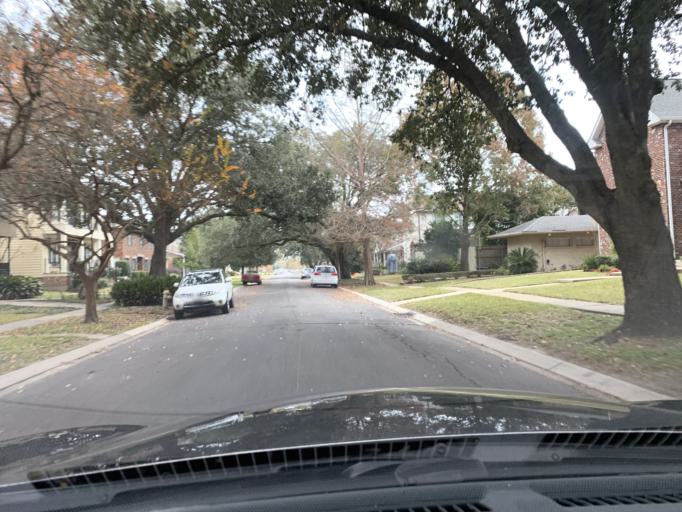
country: US
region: Louisiana
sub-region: Jefferson Parish
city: Metairie
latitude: 30.0088
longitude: -90.1010
